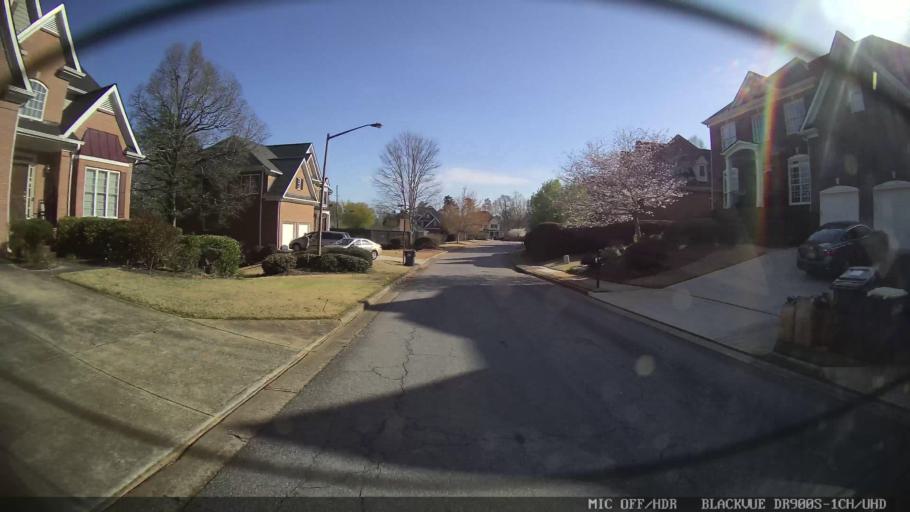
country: US
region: Georgia
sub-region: Cobb County
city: Marietta
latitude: 33.9842
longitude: -84.4885
